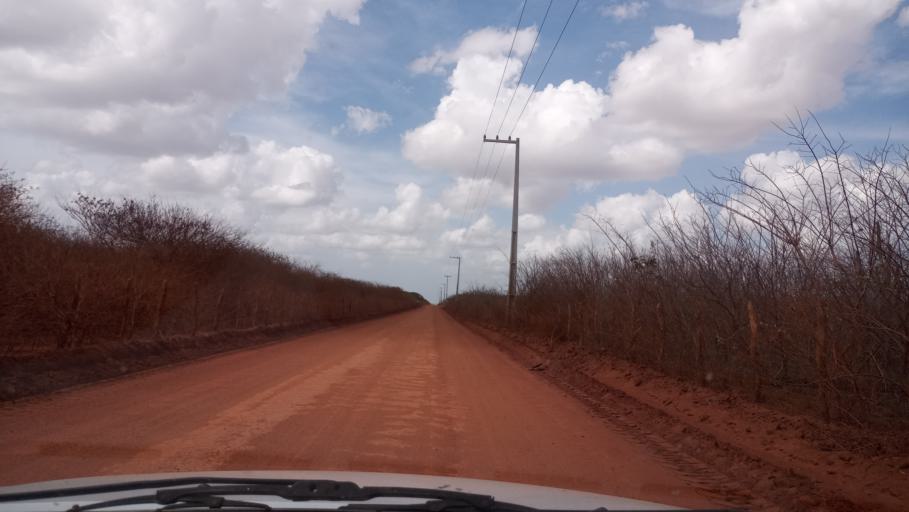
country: BR
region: Rio Grande do Norte
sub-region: Joao Camara
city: Joao Camara
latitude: -5.3598
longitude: -35.8345
